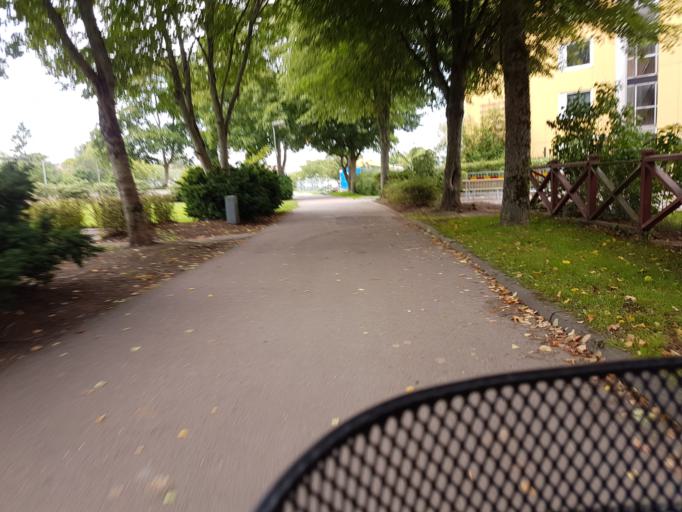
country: SE
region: Vaestra Goetaland
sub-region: Ale Kommun
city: Nodinge-Nol
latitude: 57.9151
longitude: 12.0679
